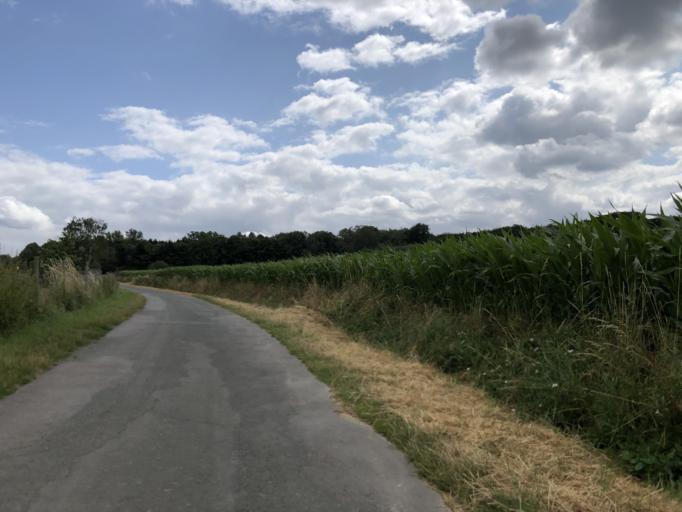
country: DE
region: North Rhine-Westphalia
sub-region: Regierungsbezirk Detmold
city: Detmold
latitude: 51.9384
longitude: 8.8408
